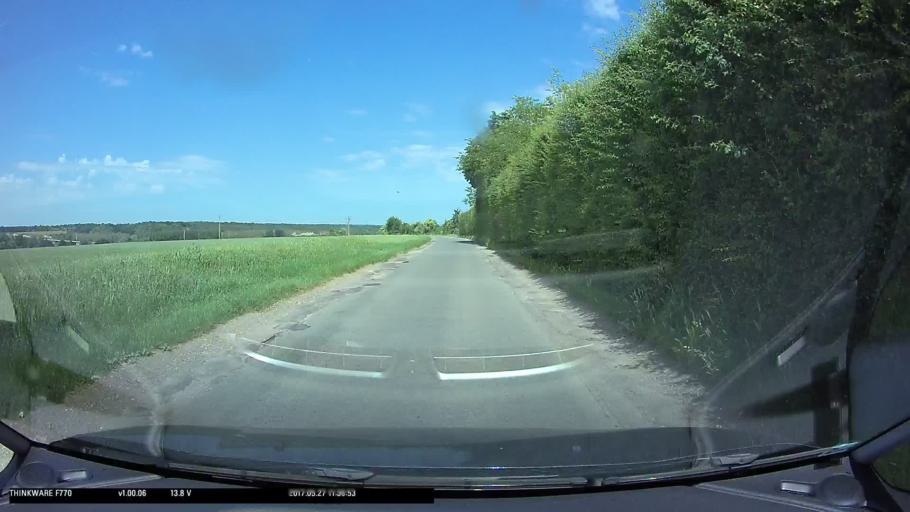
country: FR
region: Haute-Normandie
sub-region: Departement de l'Eure
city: Gisors
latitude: 49.2894
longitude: 1.7896
